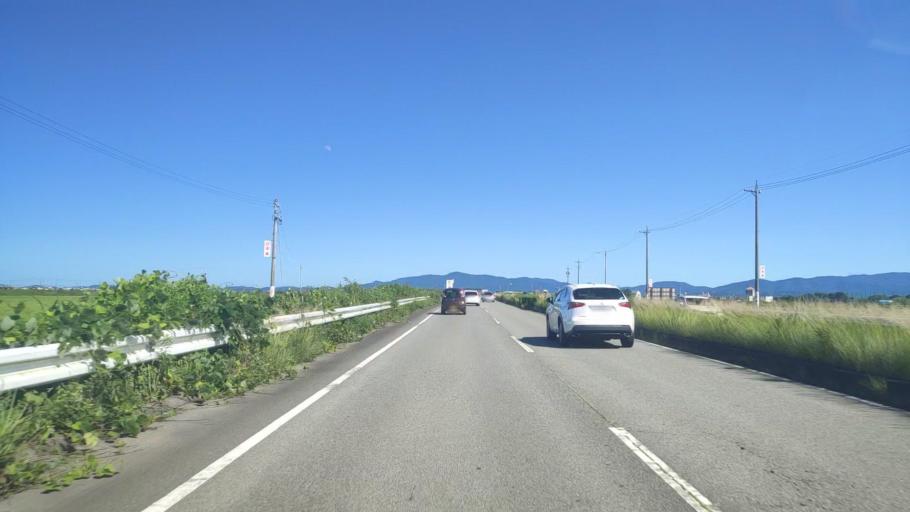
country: JP
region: Mie
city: Ise
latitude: 34.5535
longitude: 136.6542
